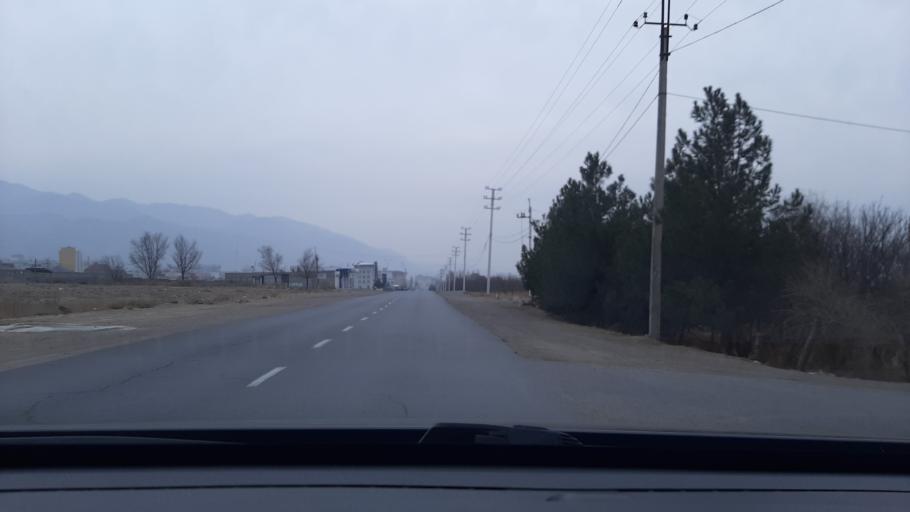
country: TJ
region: Viloyati Sughd
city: Khujand
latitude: 40.2753
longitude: 69.5792
